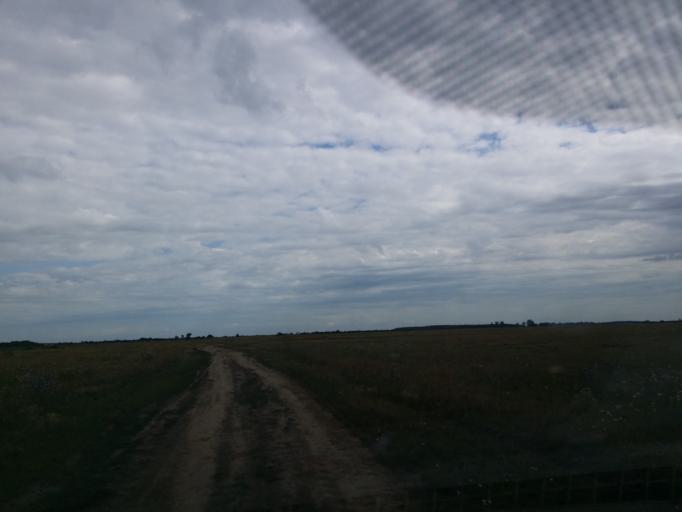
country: HU
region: Hajdu-Bihar
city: Egyek
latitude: 47.5530
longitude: 20.9421
